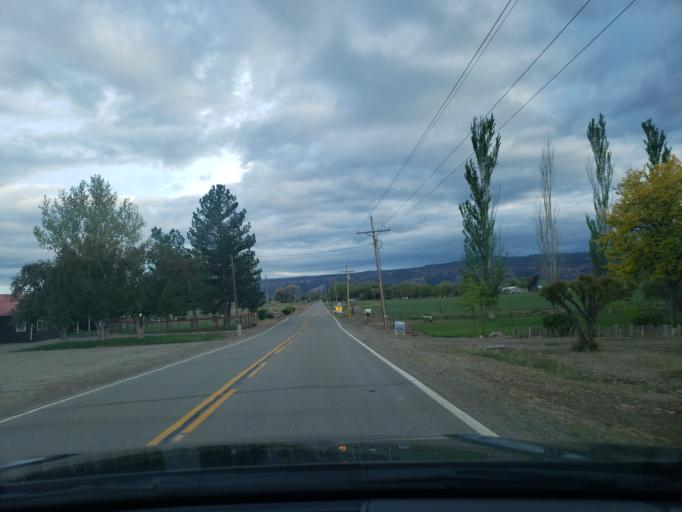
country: US
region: Colorado
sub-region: Mesa County
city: Fruita
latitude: 39.1771
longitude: -108.7013
